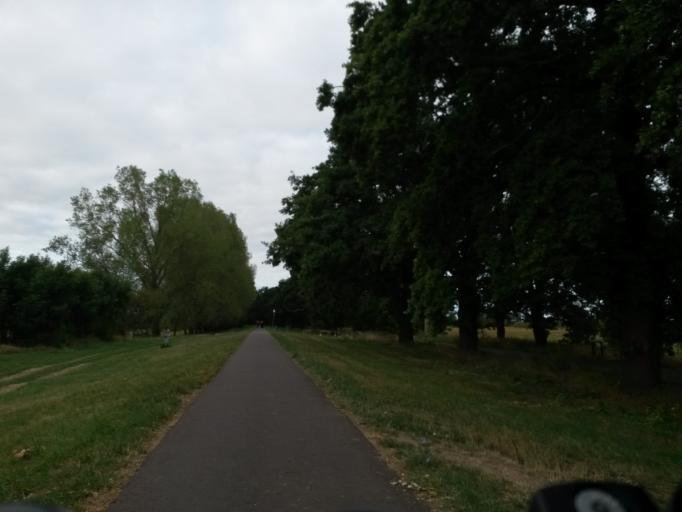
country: DE
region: Saxony-Anhalt
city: Tangermunde
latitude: 52.5351
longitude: 11.9696
